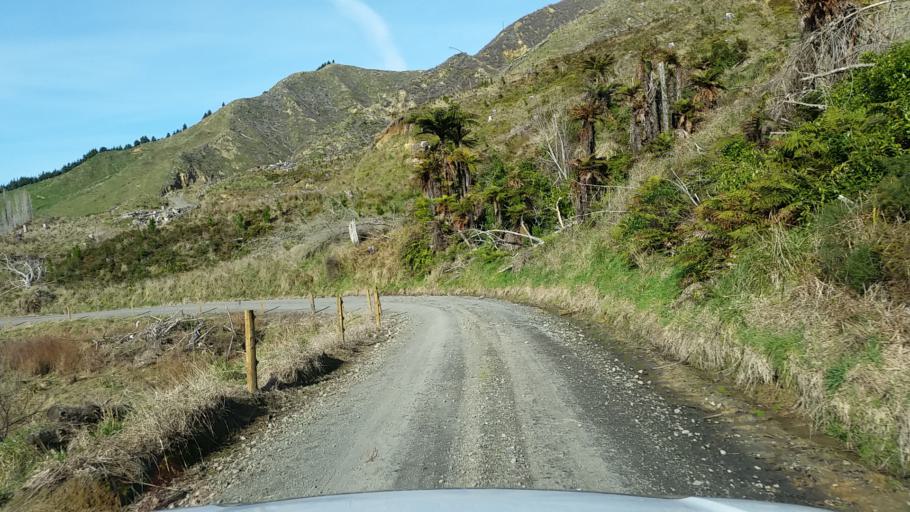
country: NZ
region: Taranaki
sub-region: South Taranaki District
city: Eltham
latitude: -39.3628
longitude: 174.5151
